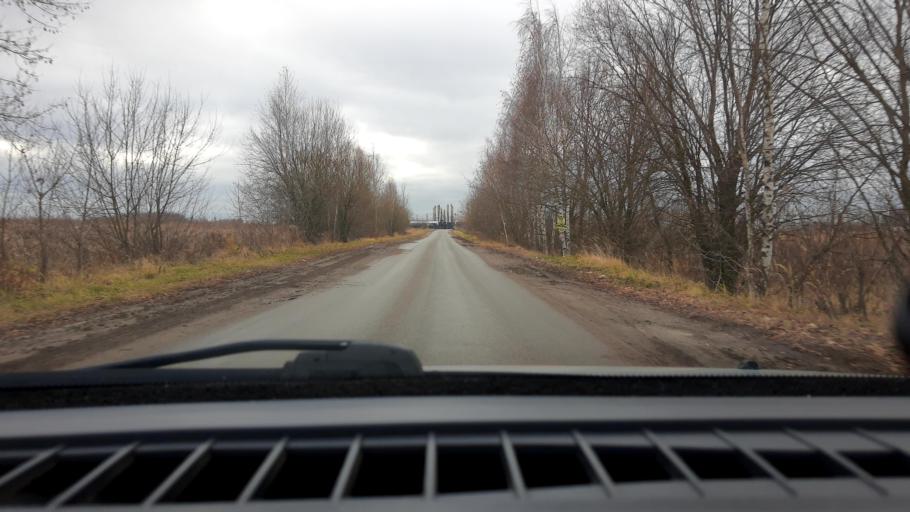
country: RU
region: Nizjnij Novgorod
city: Afonino
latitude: 56.1963
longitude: 44.1370
